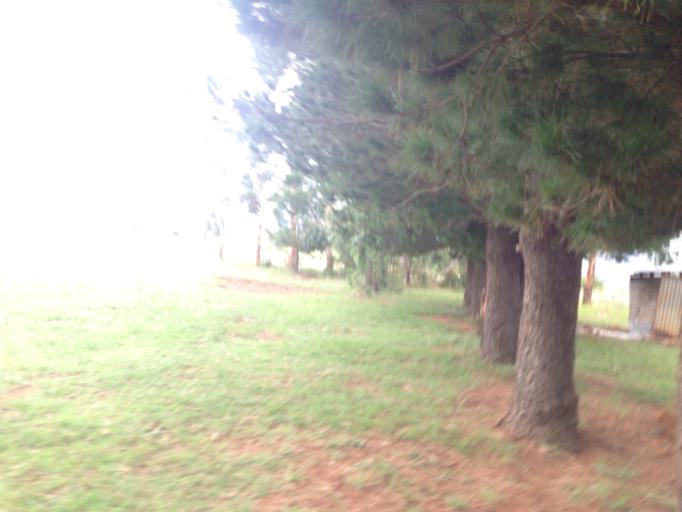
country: LS
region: Maseru
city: Nako
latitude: -29.5891
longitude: 27.7582
